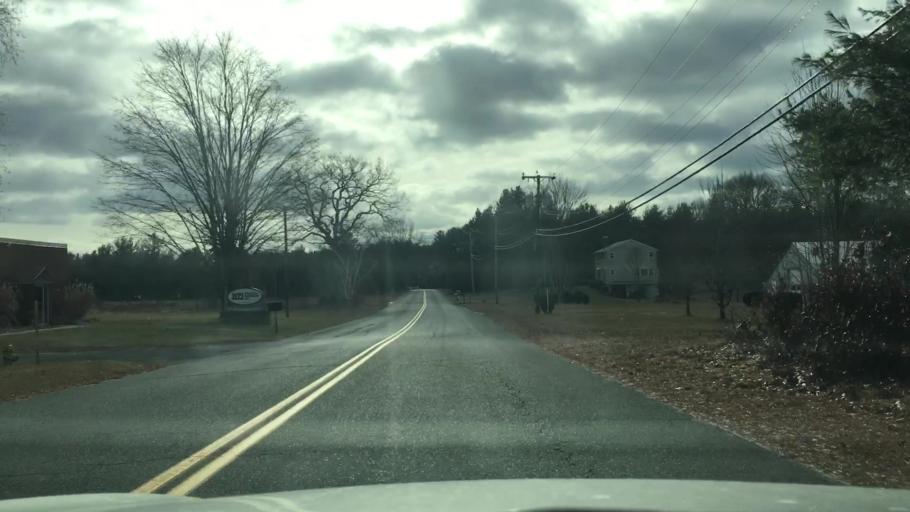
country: US
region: Massachusetts
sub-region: Hampden County
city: Southwick
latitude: 42.0690
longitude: -72.7455
